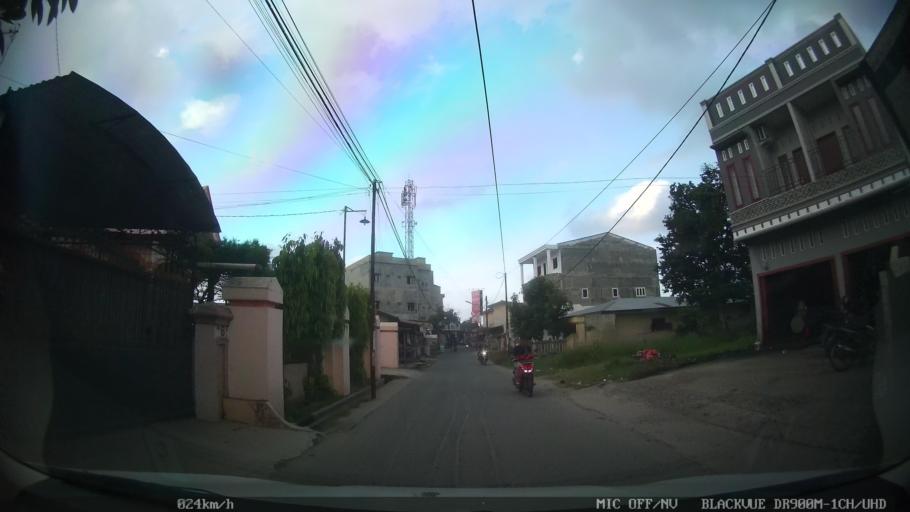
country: ID
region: North Sumatra
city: Medan
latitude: 3.5946
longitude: 98.7439
